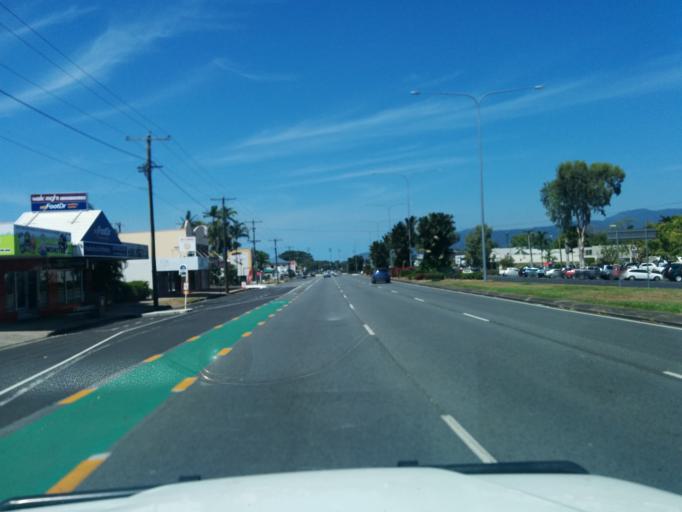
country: AU
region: Queensland
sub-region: Cairns
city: Woree
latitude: -16.9424
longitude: 145.7392
